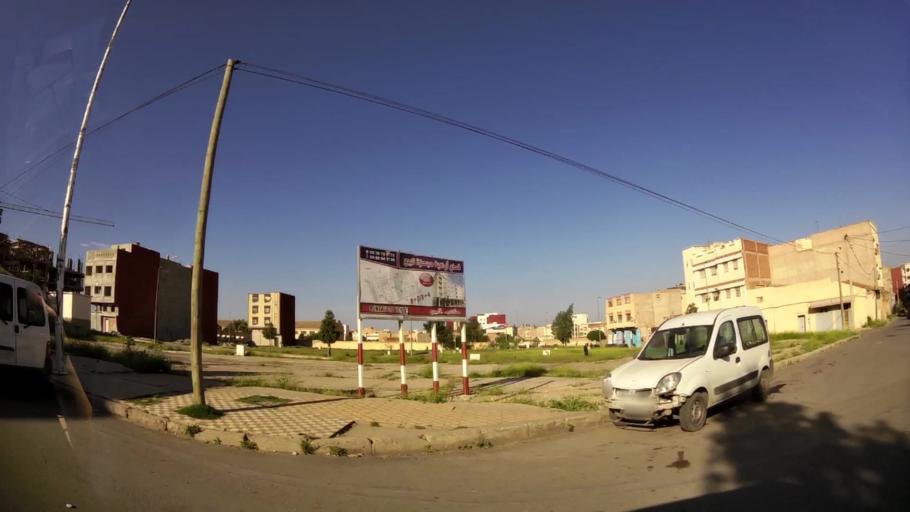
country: MA
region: Oriental
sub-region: Oujda-Angad
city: Oujda
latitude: 34.6940
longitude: -1.9082
